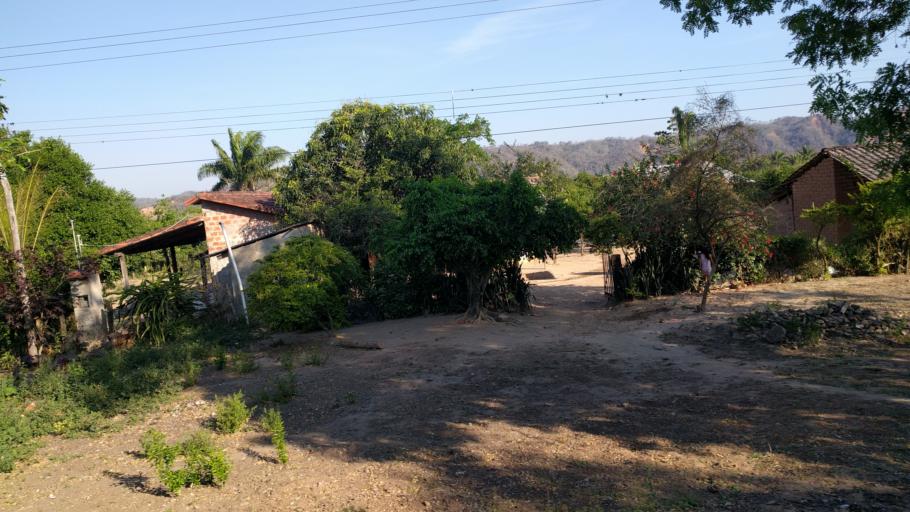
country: BO
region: Santa Cruz
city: Jorochito
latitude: -18.1494
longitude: -63.4884
